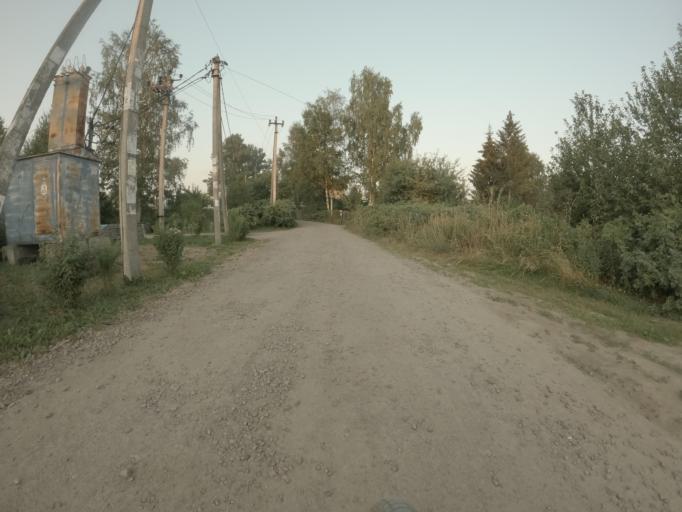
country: RU
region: Leningrad
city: Imeni Sverdlova
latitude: 59.7859
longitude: 30.7161
